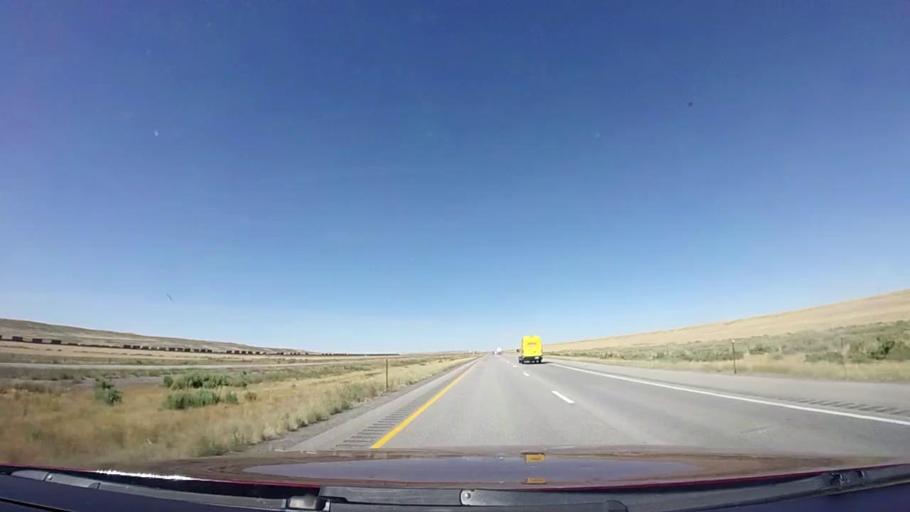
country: US
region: Wyoming
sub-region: Carbon County
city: Rawlins
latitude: 41.6584
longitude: -108.0846
